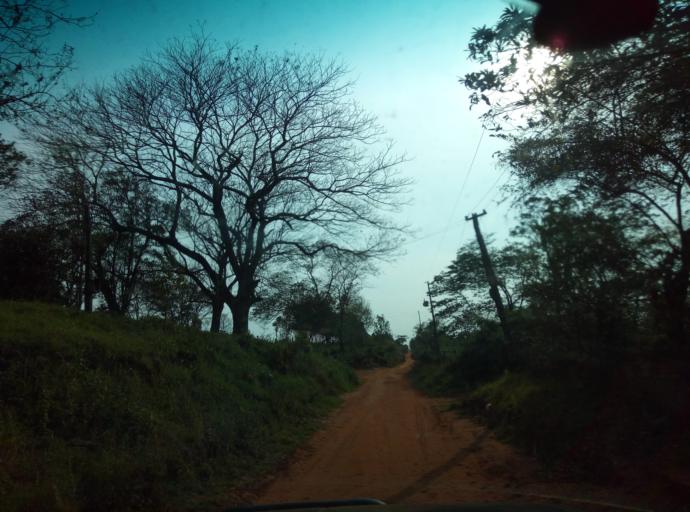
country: PY
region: Caaguazu
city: San Joaquin
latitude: -25.1498
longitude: -56.1018
